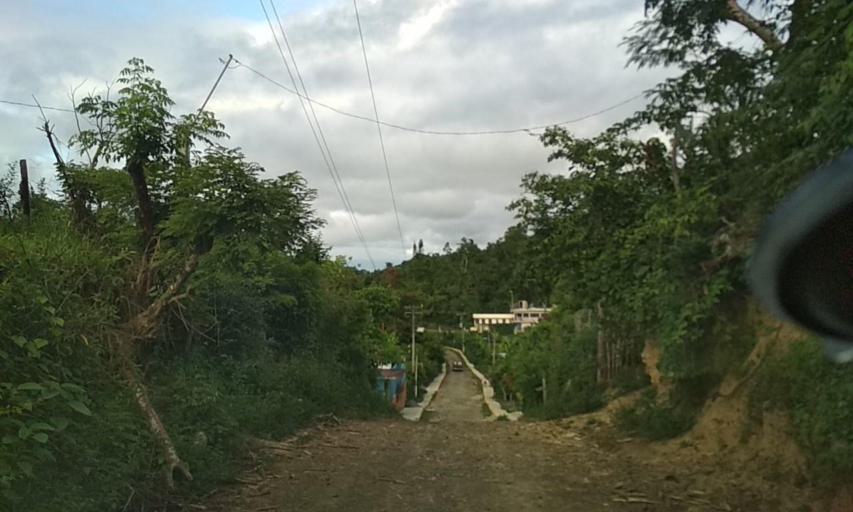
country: MX
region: Veracruz
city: Cazones de Herrera
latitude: 20.6397
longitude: -97.3403
